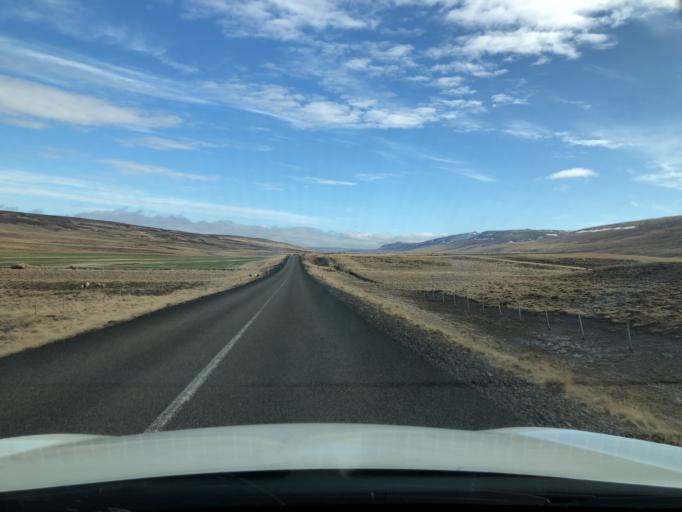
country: IS
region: West
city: Borgarnes
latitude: 65.1157
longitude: -21.6795
